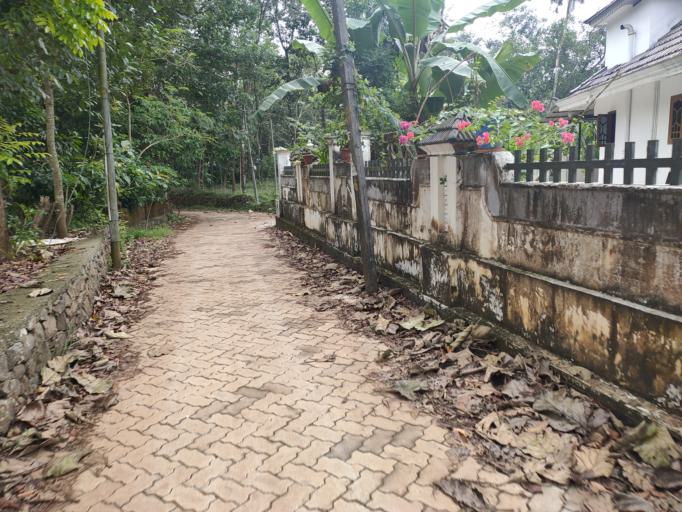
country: IN
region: Kerala
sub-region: Ernakulam
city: Kotamangalam
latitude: 10.0009
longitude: 76.6389
